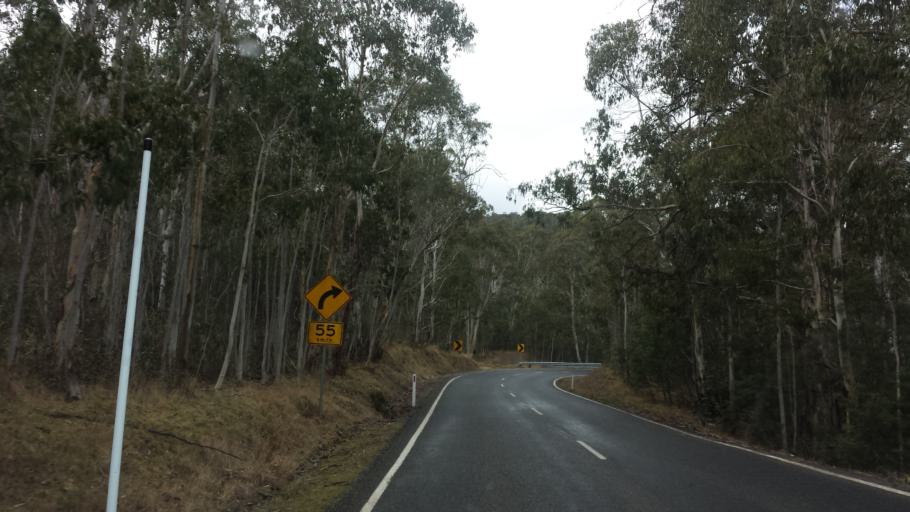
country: AU
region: Victoria
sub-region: Alpine
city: Mount Beauty
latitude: -37.1324
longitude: 147.4988
